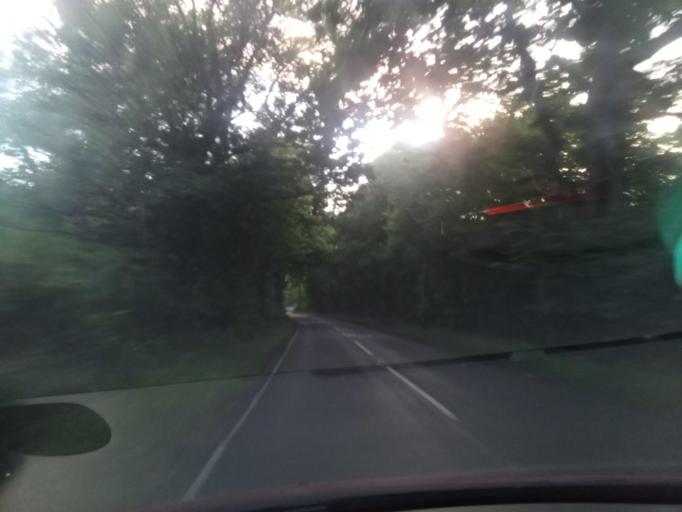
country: GB
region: England
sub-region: Northumberland
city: Bardon Mill
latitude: 54.8928
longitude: -2.3509
